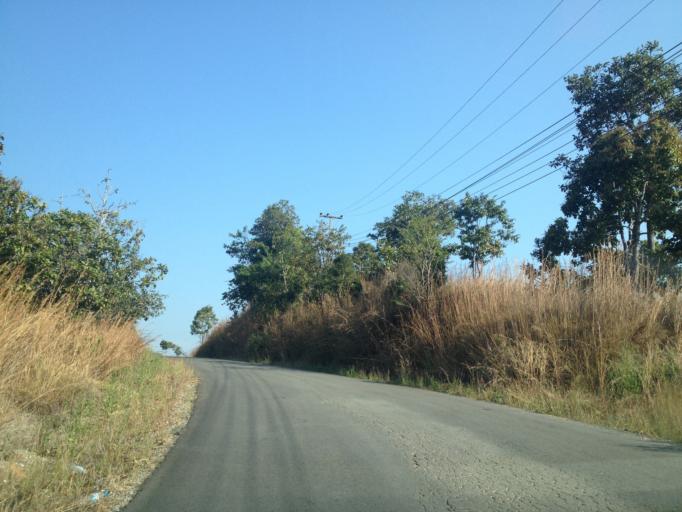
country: TH
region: Mae Hong Son
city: Ban Huai I Huak
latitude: 18.1454
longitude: 98.2184
